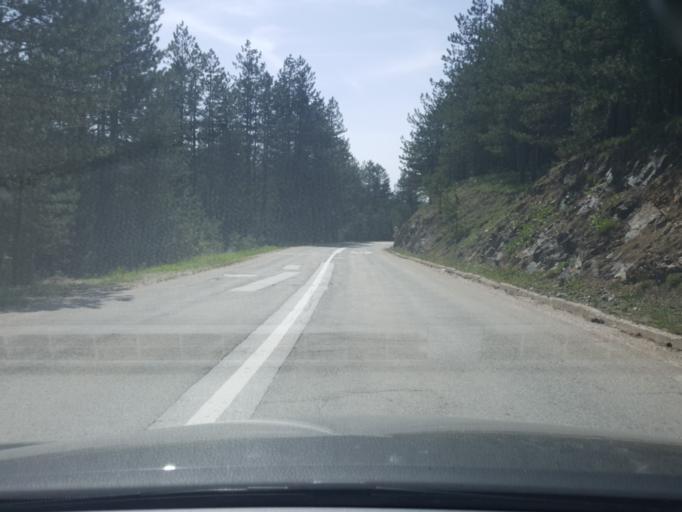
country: RS
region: Central Serbia
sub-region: Zlatiborski Okrug
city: Cajetina
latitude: 43.8336
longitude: 19.6368
